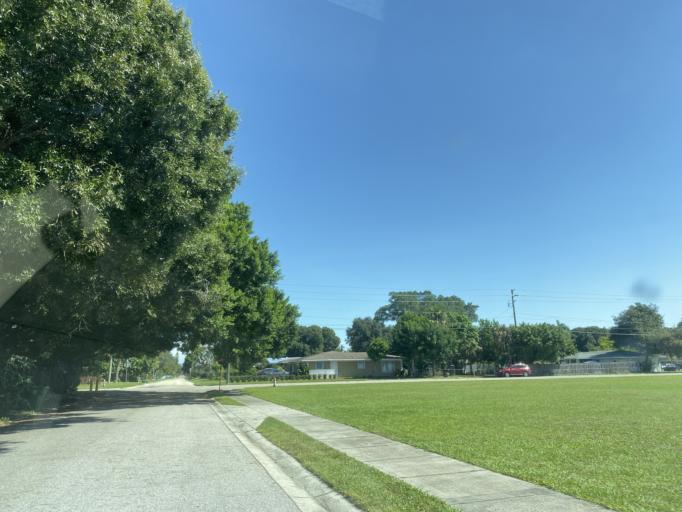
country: US
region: Florida
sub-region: Manatee County
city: South Bradenton
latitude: 27.4810
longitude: -82.5883
